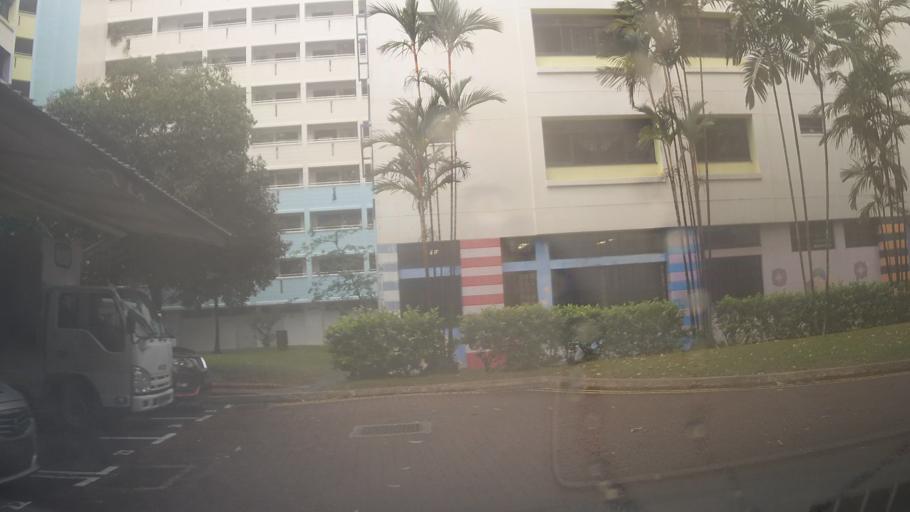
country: MY
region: Johor
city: Johor Bahru
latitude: 1.4410
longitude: 103.7964
